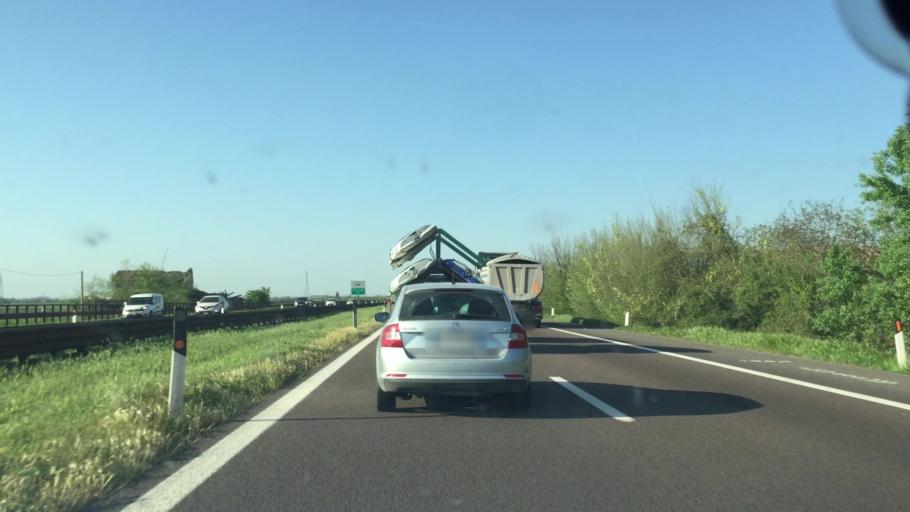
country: IT
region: Emilia-Romagna
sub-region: Provincia di Modena
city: Migliarina
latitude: 44.8190
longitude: 10.8514
